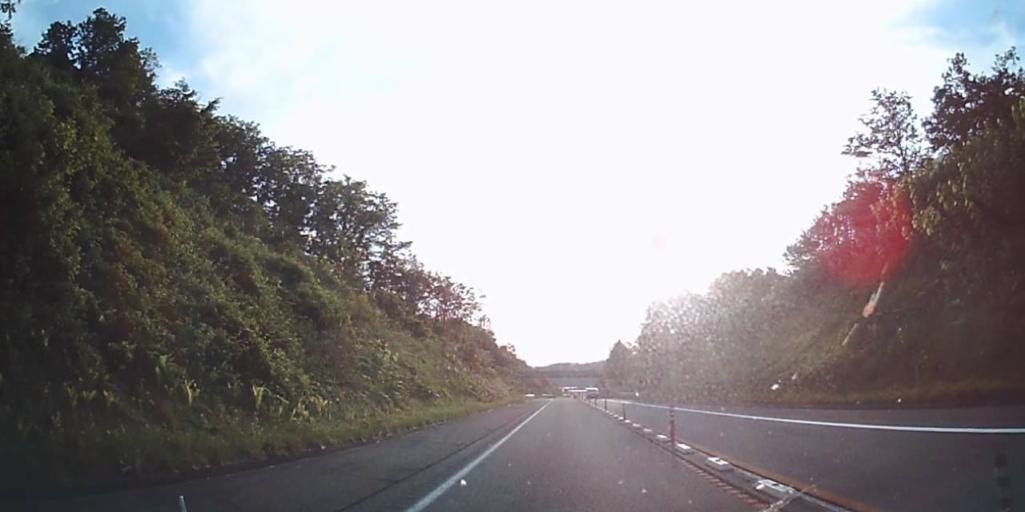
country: JP
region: Hokkaido
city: Date
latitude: 42.4974
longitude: 140.8629
